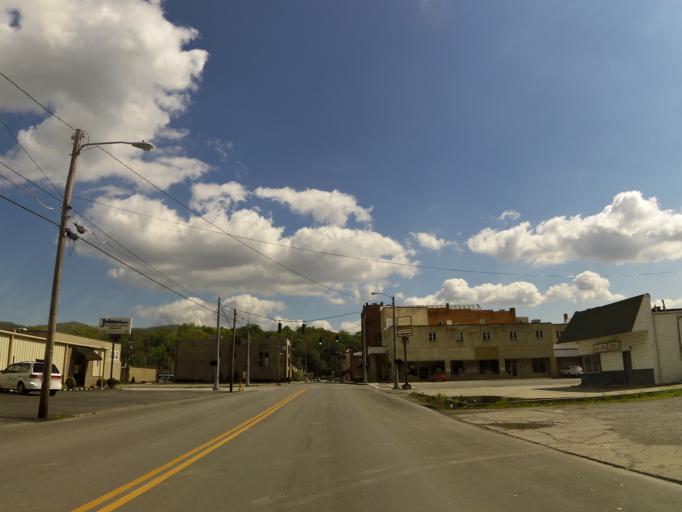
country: US
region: Kentucky
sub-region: Bell County
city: Middlesboro
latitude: 36.6093
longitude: -83.7129
